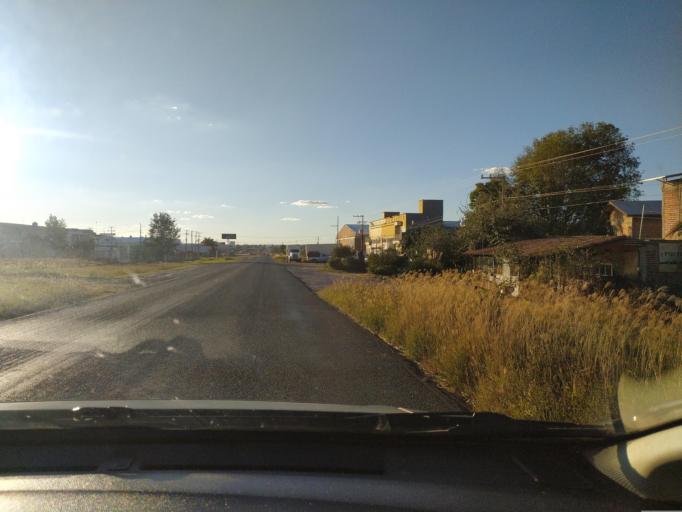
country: MX
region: Jalisco
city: San Julian
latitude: 21.0072
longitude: -102.1404
